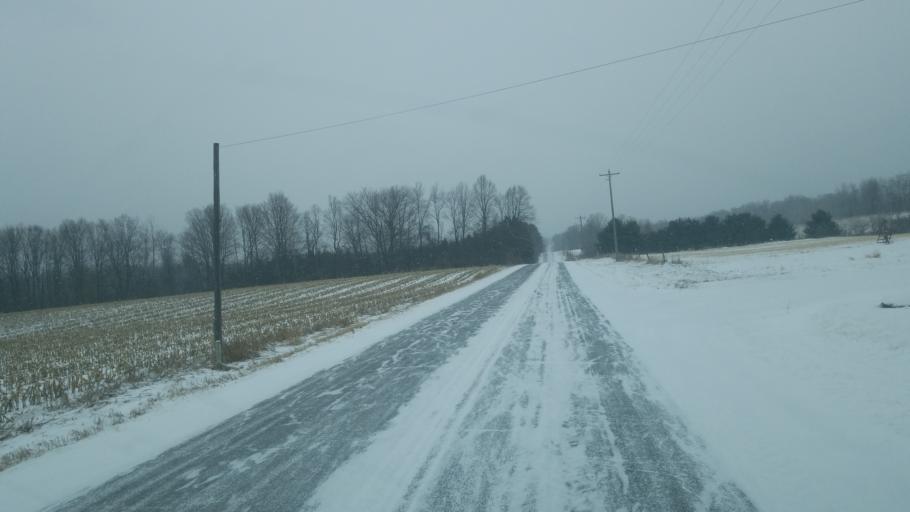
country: US
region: Michigan
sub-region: Mecosta County
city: Big Rapids
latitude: 43.7842
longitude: -85.4026
